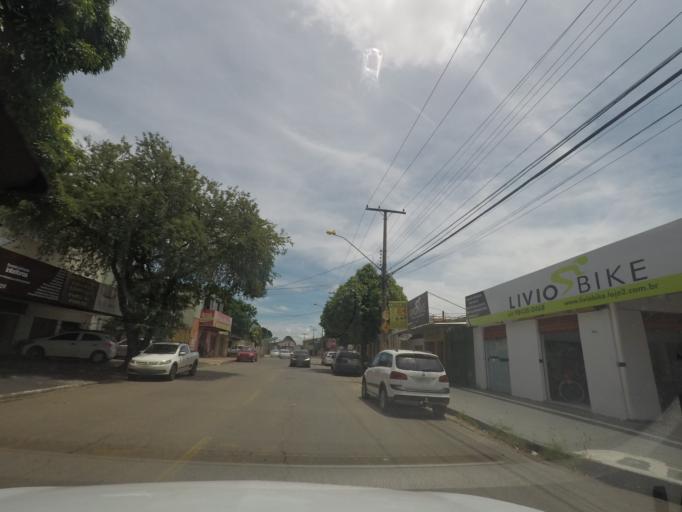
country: BR
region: Goias
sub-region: Goiania
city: Goiania
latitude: -16.6826
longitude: -49.2832
